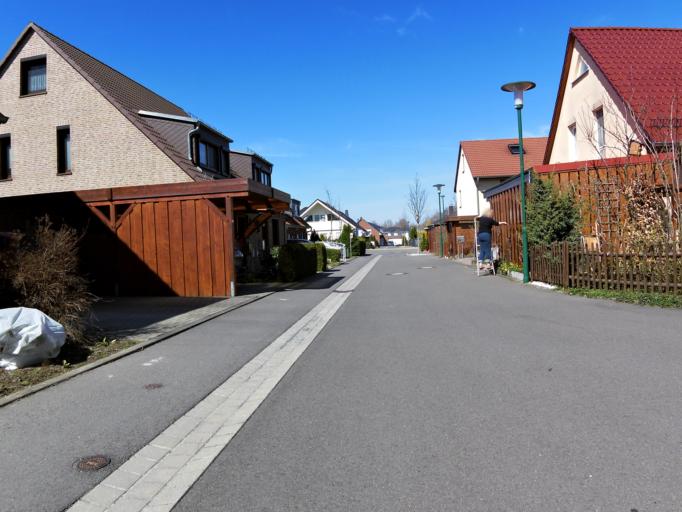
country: DE
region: Saxony
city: Taucha
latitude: 51.3614
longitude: 12.4753
